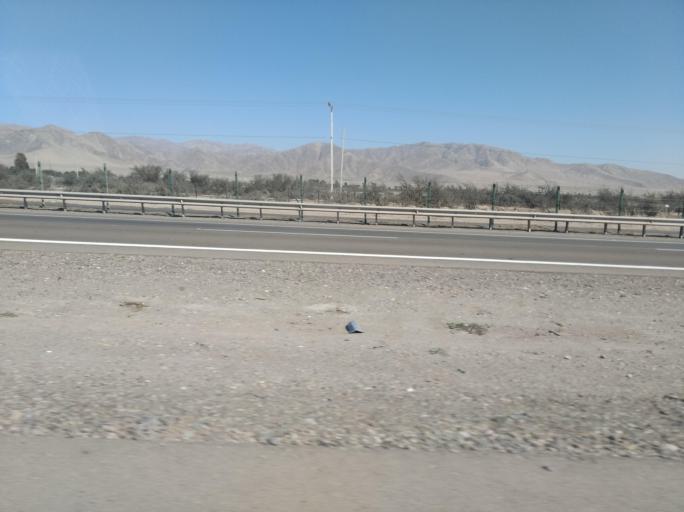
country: CL
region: Atacama
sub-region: Provincia de Copiapo
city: Copiapo
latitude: -27.3285
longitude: -70.5622
